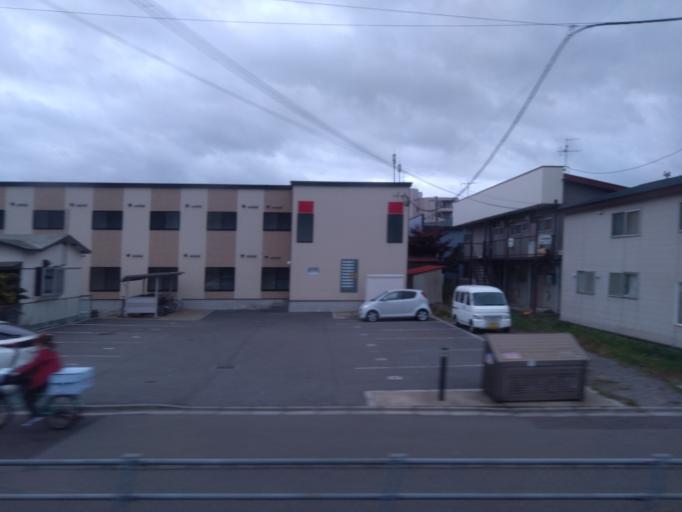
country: JP
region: Hokkaido
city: Hakodate
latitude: 41.7927
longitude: 140.7313
